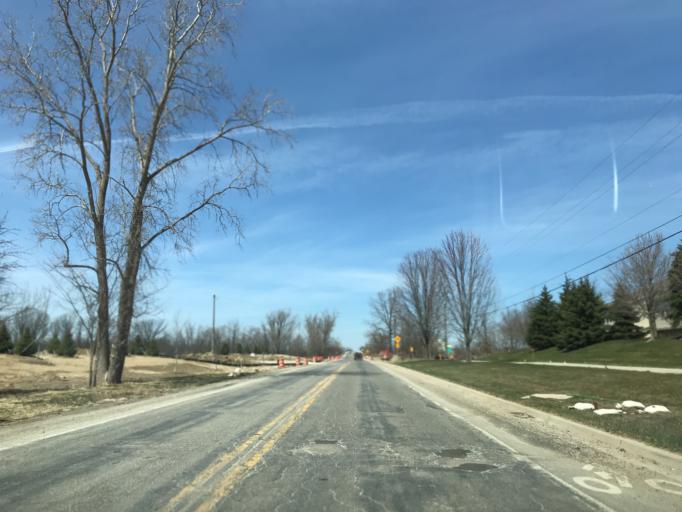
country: US
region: Michigan
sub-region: Washtenaw County
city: Ann Arbor
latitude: 42.3200
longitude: -83.7077
